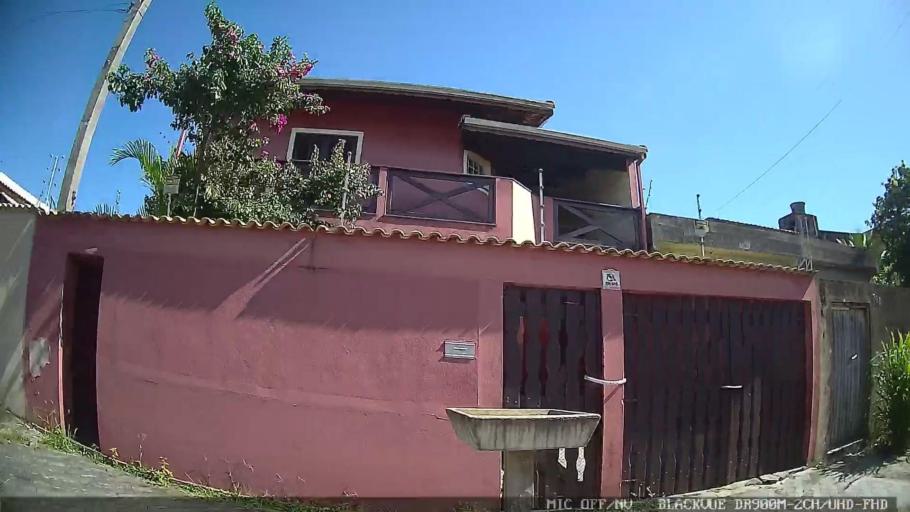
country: BR
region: Sao Paulo
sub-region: Peruibe
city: Peruibe
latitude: -24.2753
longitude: -46.9417
